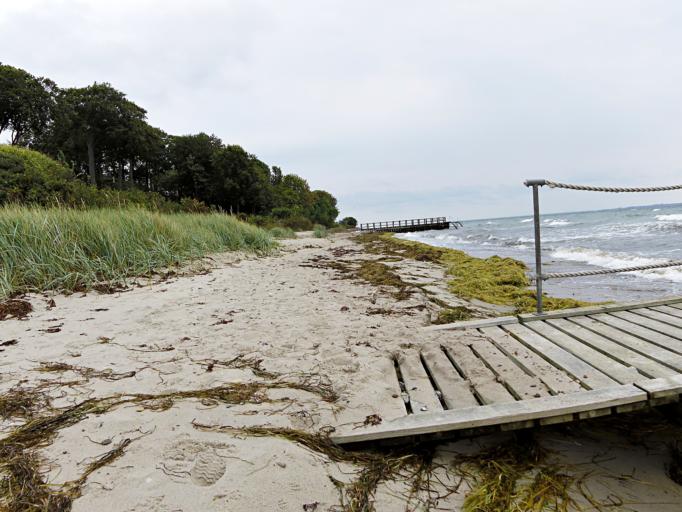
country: DK
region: Capital Region
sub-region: Rudersdal Kommune
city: Trorod
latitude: 55.8374
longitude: 12.5742
